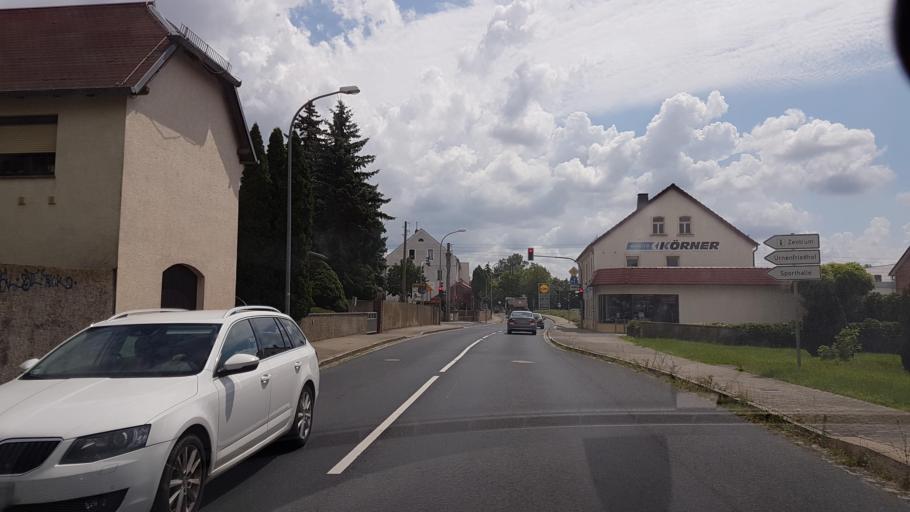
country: DE
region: Saxony
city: Nunchritz
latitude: 51.3015
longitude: 13.3826
